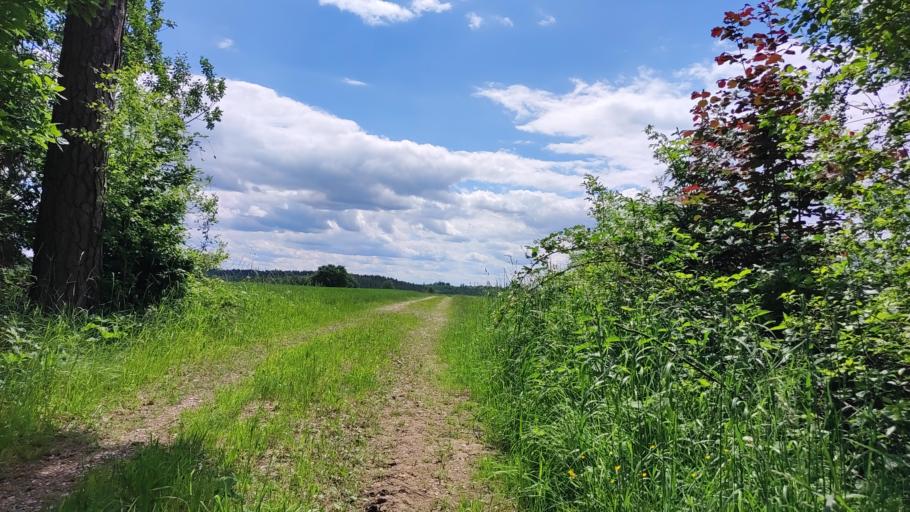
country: DE
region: Bavaria
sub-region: Swabia
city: Landensberg
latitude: 48.3866
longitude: 10.5353
